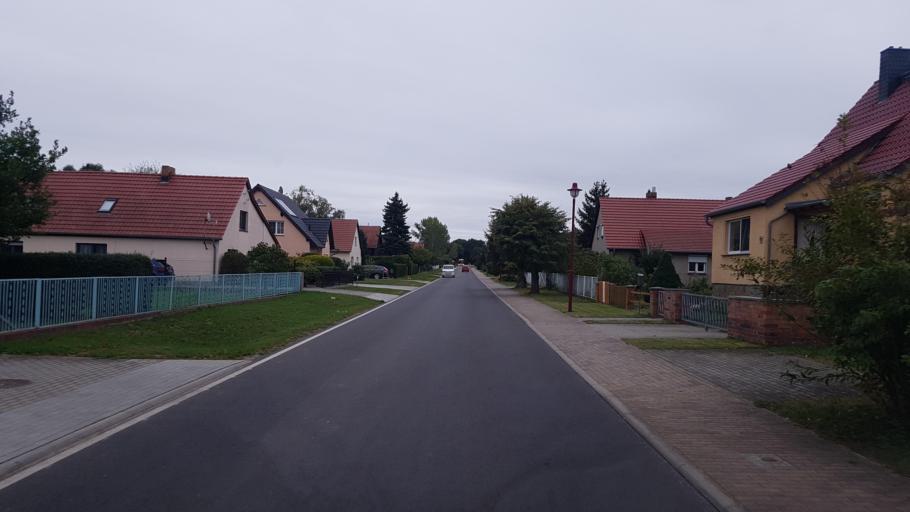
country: DE
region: Brandenburg
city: Kasel-Golzig
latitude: 51.8925
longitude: 13.6482
